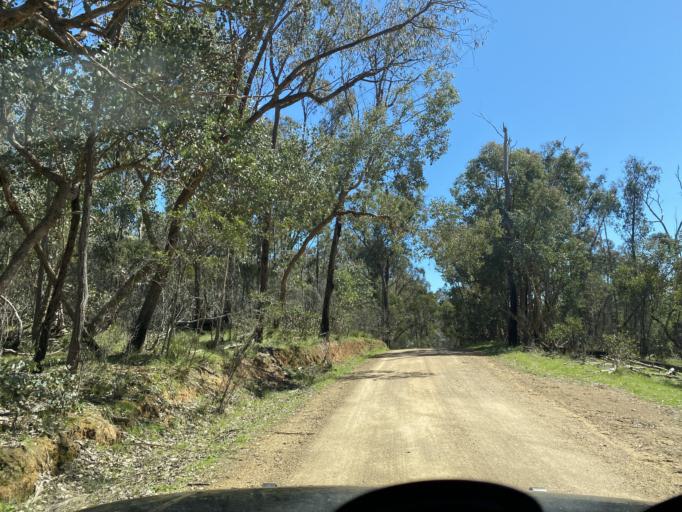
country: AU
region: Victoria
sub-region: Benalla
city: Benalla
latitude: -36.7072
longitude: 146.1781
